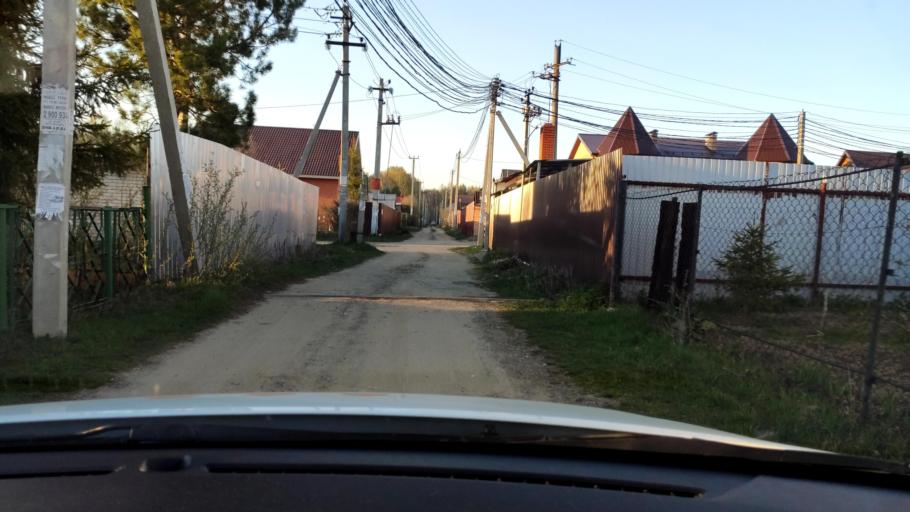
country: RU
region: Tatarstan
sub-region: Gorod Kazan'
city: Kazan
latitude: 55.9225
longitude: 49.1488
